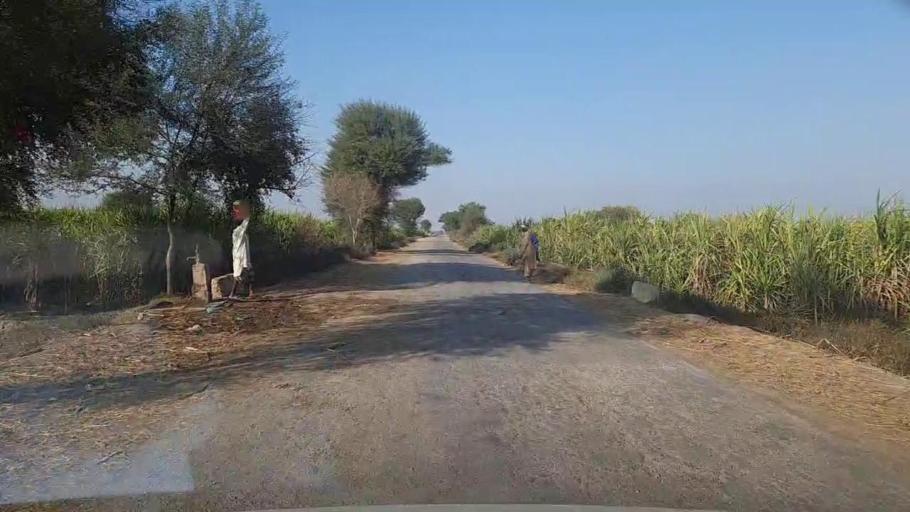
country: PK
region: Sindh
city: Phulji
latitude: 26.8498
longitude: 67.7937
